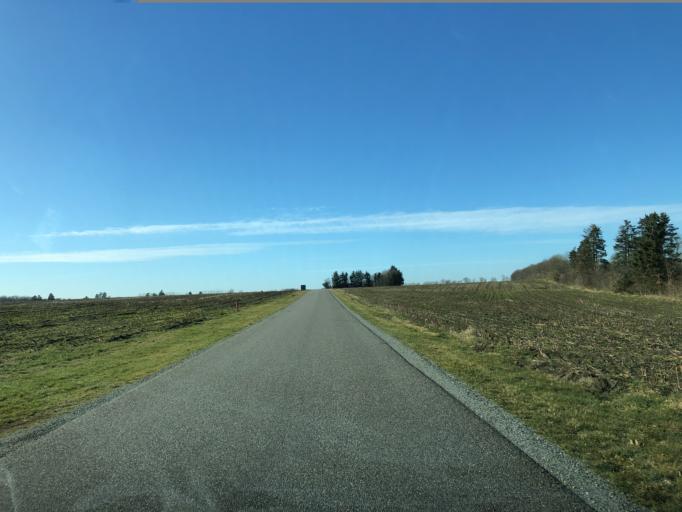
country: DK
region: Central Jutland
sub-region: Ikast-Brande Kommune
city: Bording Kirkeby
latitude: 56.1549
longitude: 9.2594
